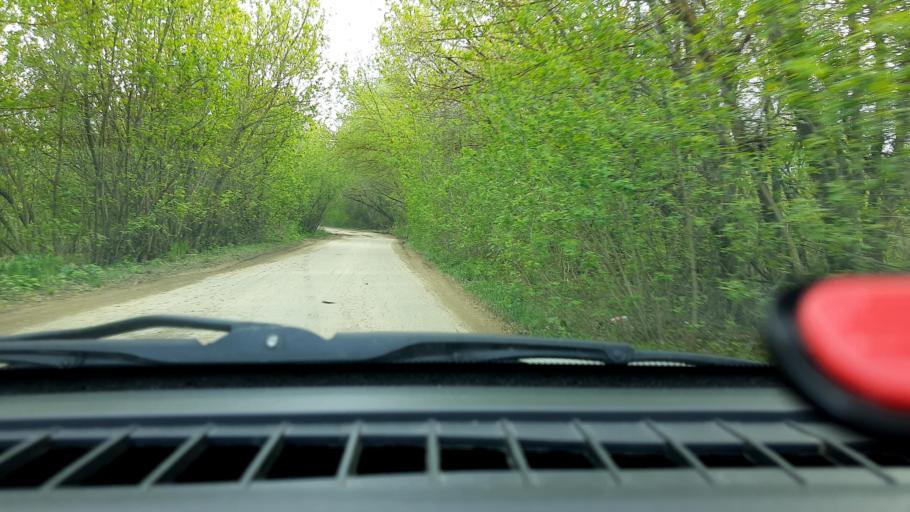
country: RU
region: Nizjnij Novgorod
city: Neklyudovo
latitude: 56.3903
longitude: 43.8430
